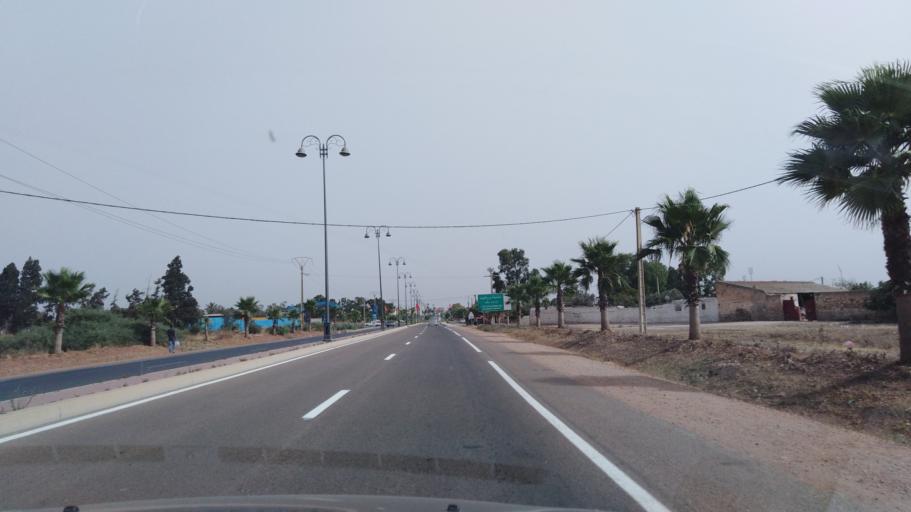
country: MA
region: Chaouia-Ouardigha
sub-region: Settat Province
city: Berrechid
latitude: 33.2879
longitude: -7.5935
